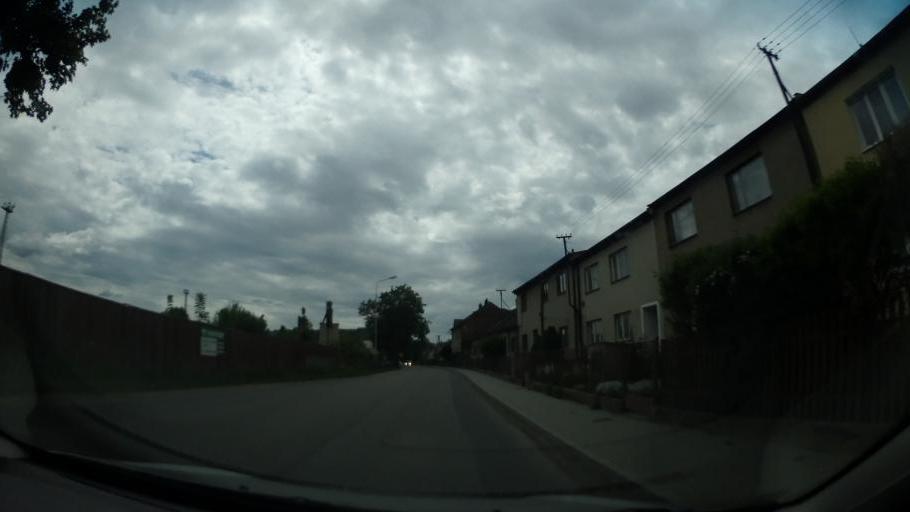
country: CZ
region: Pardubicky
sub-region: Okres Svitavy
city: Moravska Trebova
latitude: 49.7696
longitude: 16.6652
